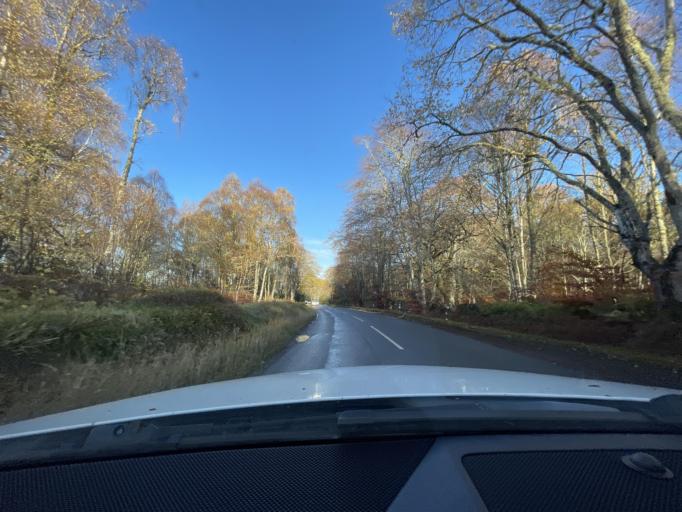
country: GB
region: Scotland
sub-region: Highland
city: Inverness
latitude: 57.4405
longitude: -4.2635
